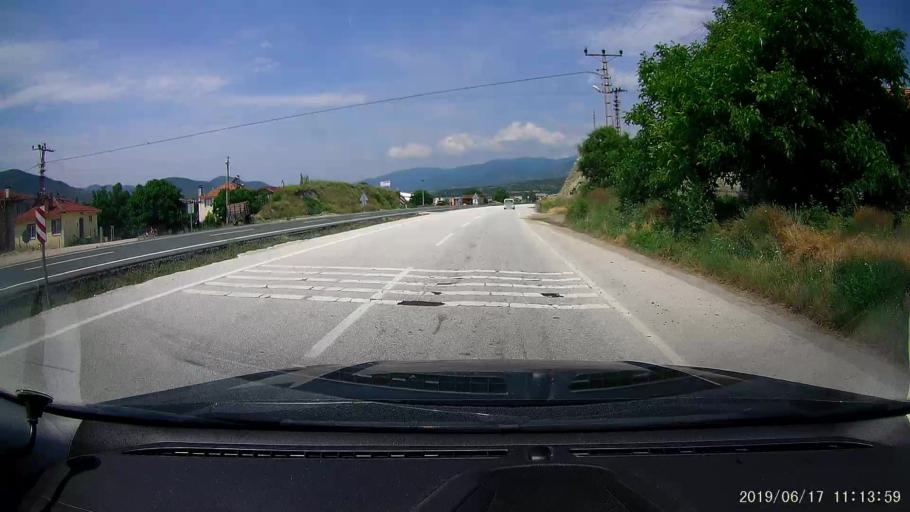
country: TR
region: Kastamonu
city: Tosya
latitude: 40.9566
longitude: 33.9596
